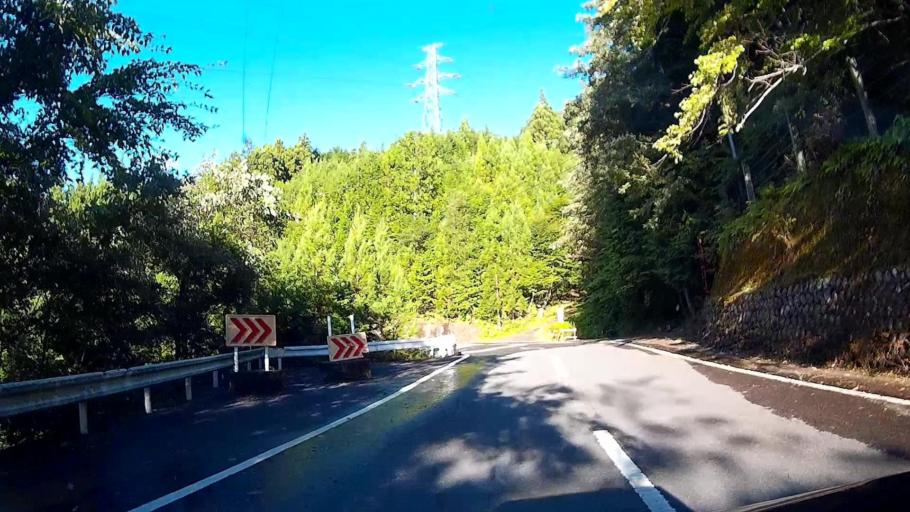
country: JP
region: Shizuoka
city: Shizuoka-shi
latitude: 35.1999
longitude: 138.2477
